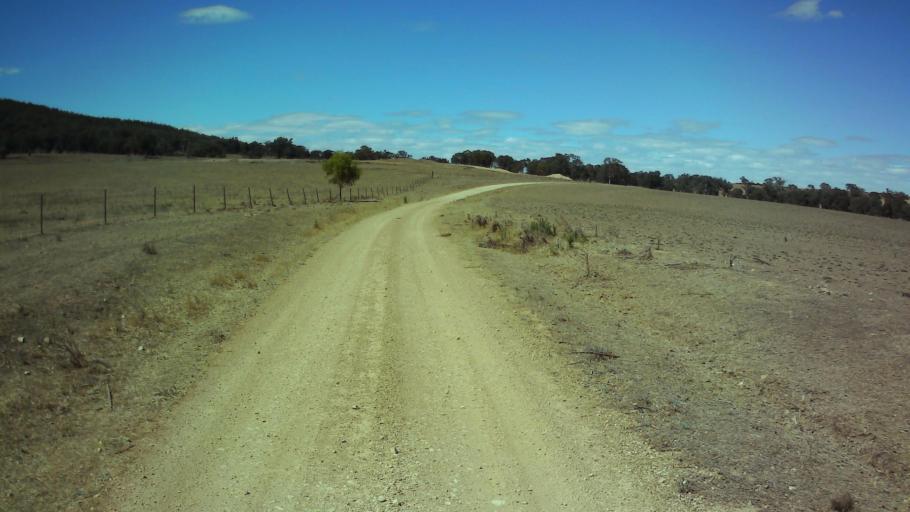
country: AU
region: New South Wales
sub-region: Young
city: Young
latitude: -34.0402
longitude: 148.4311
